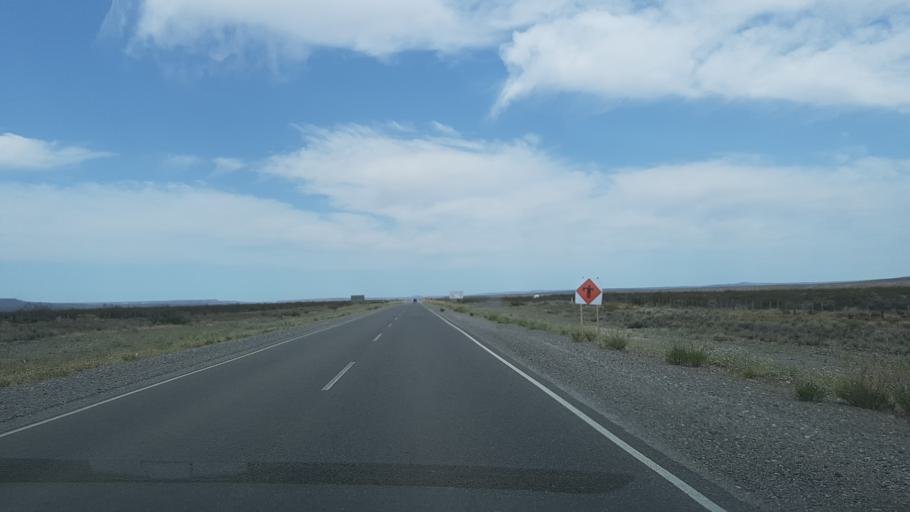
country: AR
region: Neuquen
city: Piedra del Aguila
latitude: -39.8171
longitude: -69.7282
